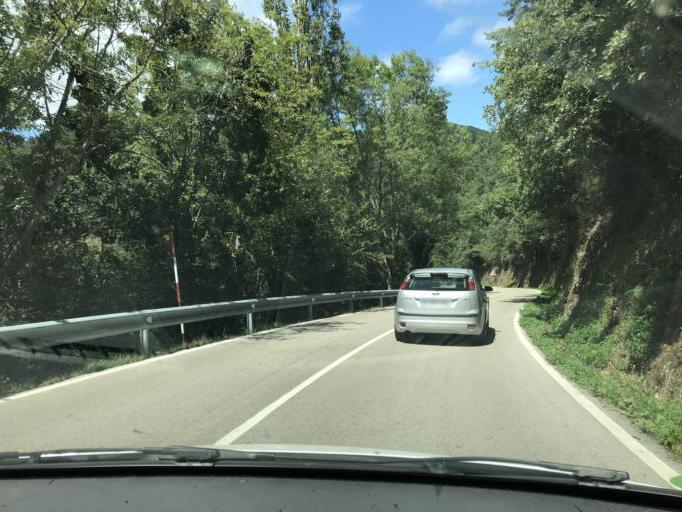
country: ES
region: Cantabria
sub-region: Provincia de Cantabria
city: Cabezon de Liebana
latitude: 43.0738
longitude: -4.4967
